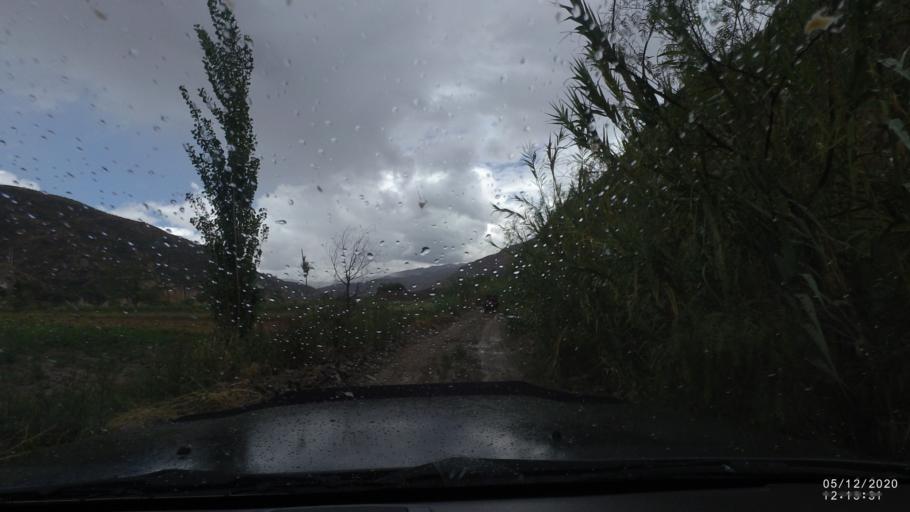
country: BO
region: Cochabamba
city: Sipe Sipe
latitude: -17.5608
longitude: -66.3792
